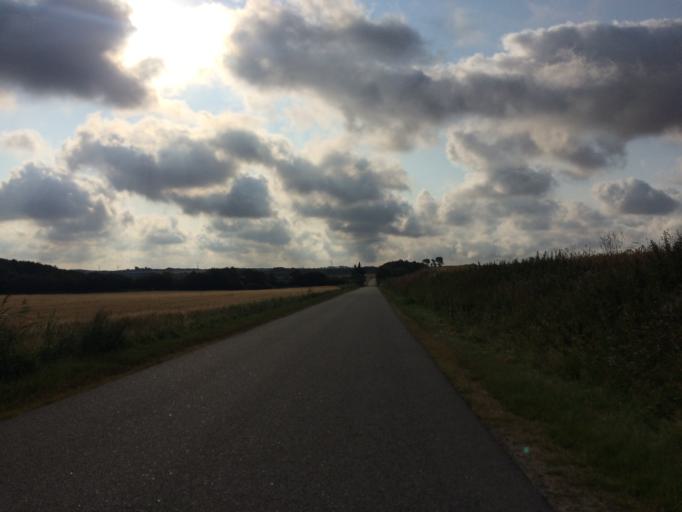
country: DK
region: Central Jutland
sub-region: Holstebro Kommune
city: Vinderup
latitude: 56.6137
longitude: 8.7654
